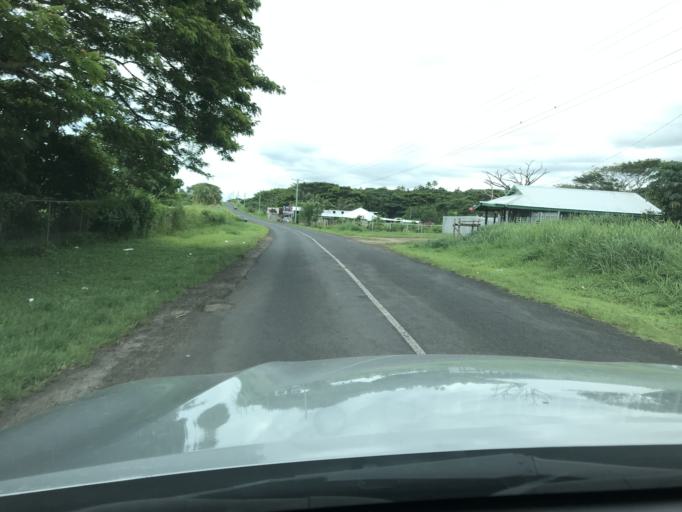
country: WS
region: Aiga-i-le-Tai
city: Mulifanua
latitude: -13.8319
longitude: -172.0313
